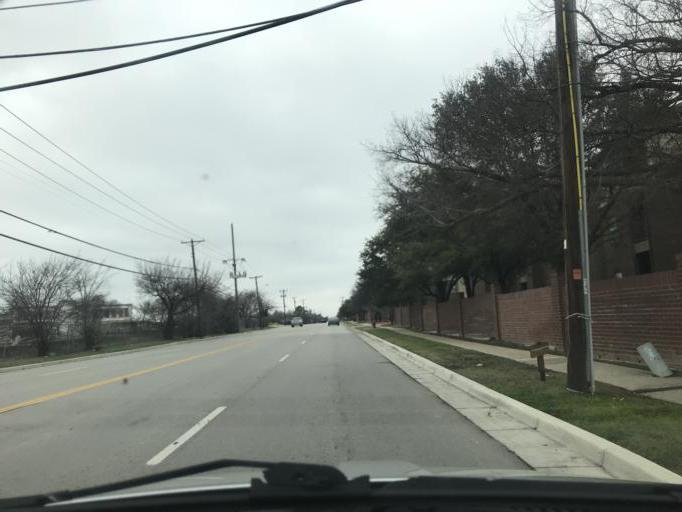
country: US
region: Texas
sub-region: Tarrant County
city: North Richland Hills
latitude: 32.8426
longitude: -97.2035
